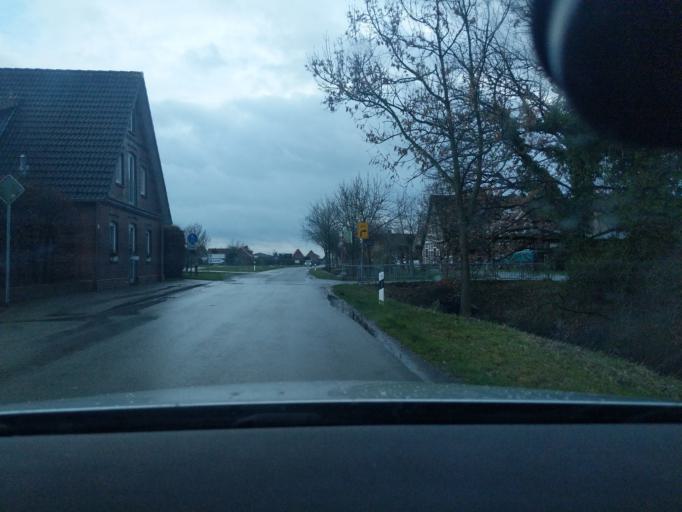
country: DE
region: Lower Saxony
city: Jork
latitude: 53.5360
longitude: 9.6534
